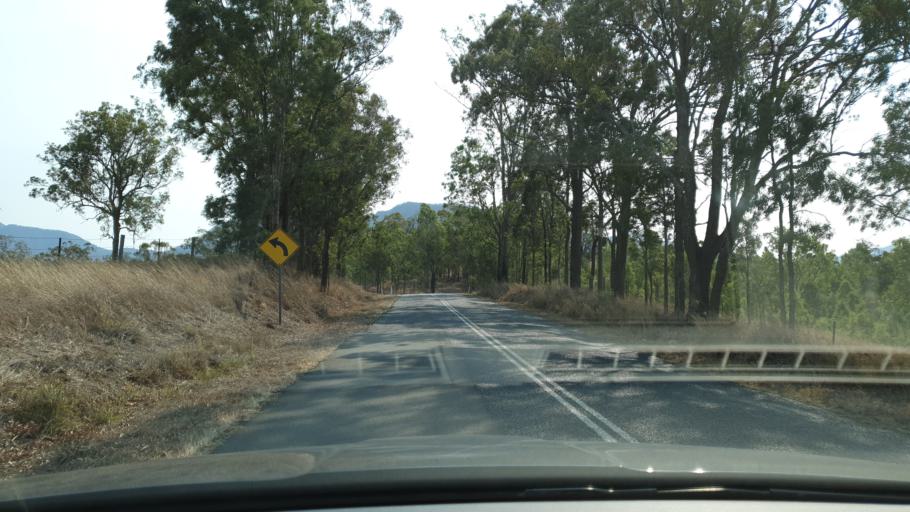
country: AU
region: Queensland
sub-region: Southern Downs
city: Warwick
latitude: -28.1750
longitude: 152.5446
